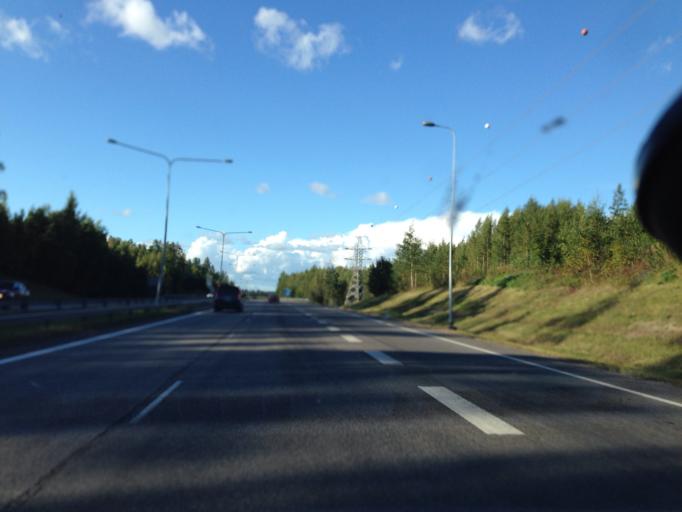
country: FI
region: Uusimaa
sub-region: Helsinki
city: Vantaa
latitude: 60.3270
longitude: 24.9985
